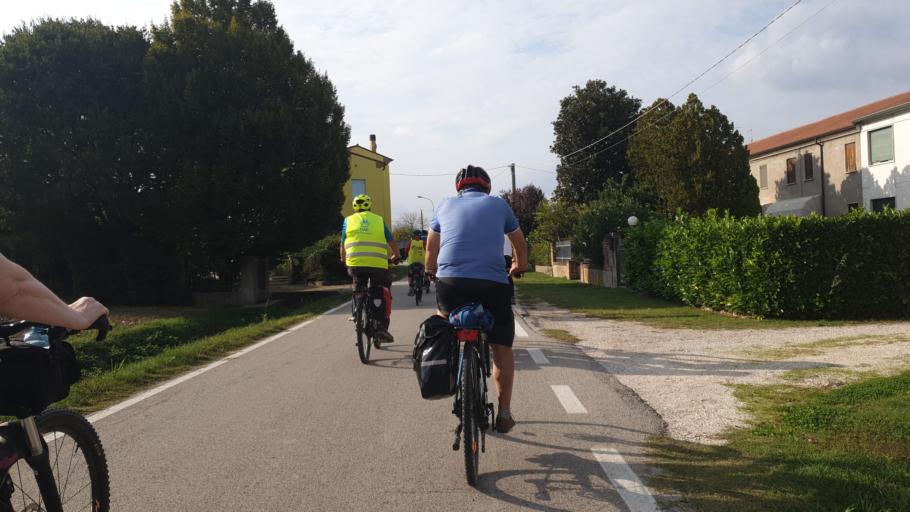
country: IT
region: Veneto
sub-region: Provincia di Vicenza
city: Poiana Maggiore
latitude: 45.2884
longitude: 11.4893
